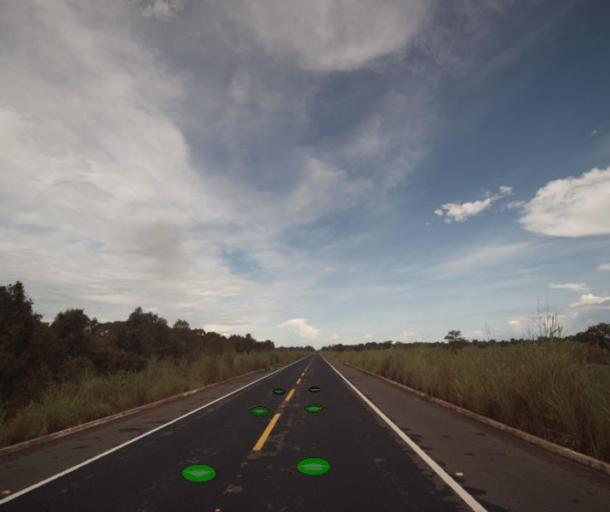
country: BR
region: Goias
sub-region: Sao Miguel Do Araguaia
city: Sao Miguel do Araguaia
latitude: -13.2433
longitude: -50.5376
